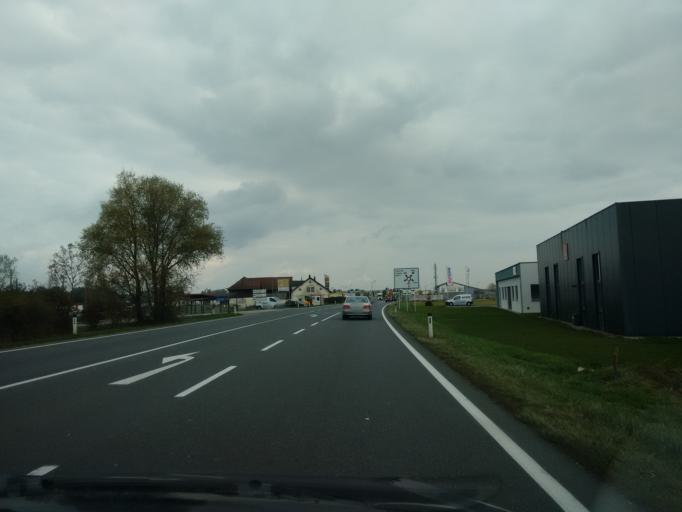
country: AT
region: Upper Austria
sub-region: Politischer Bezirk Vocklabruck
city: Oberndorf bei Schwanenstadt
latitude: 48.0458
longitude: 13.7575
